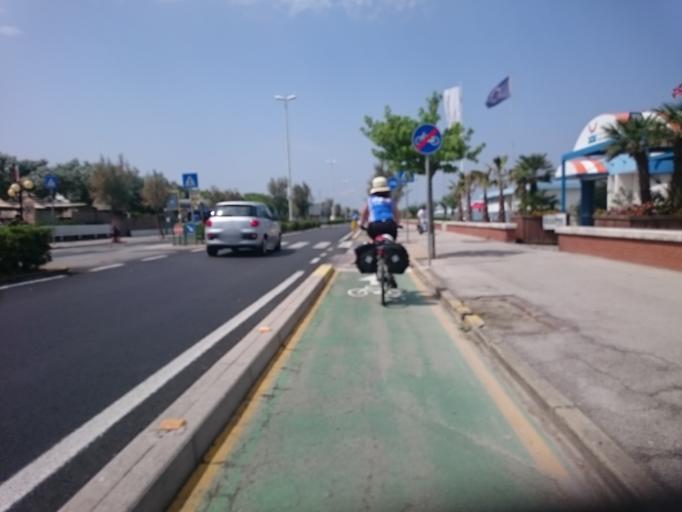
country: IT
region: Veneto
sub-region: Provincia di Venezia
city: Chioggia
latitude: 45.2031
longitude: 12.3000
